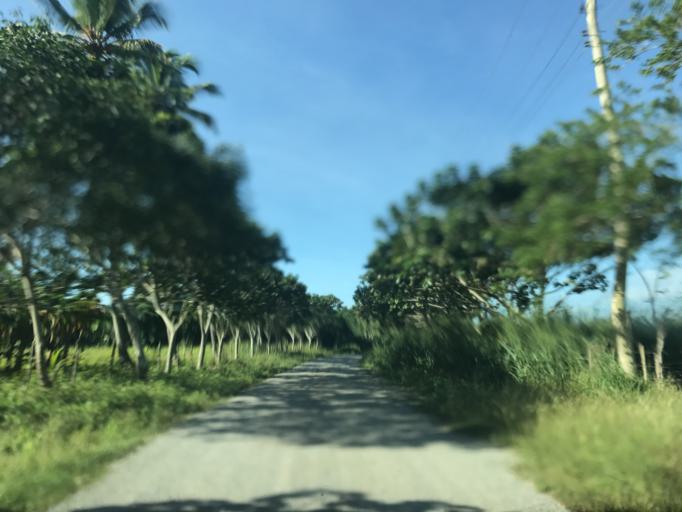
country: CU
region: Camaguey
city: Florida
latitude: 21.4825
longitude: -78.1760
